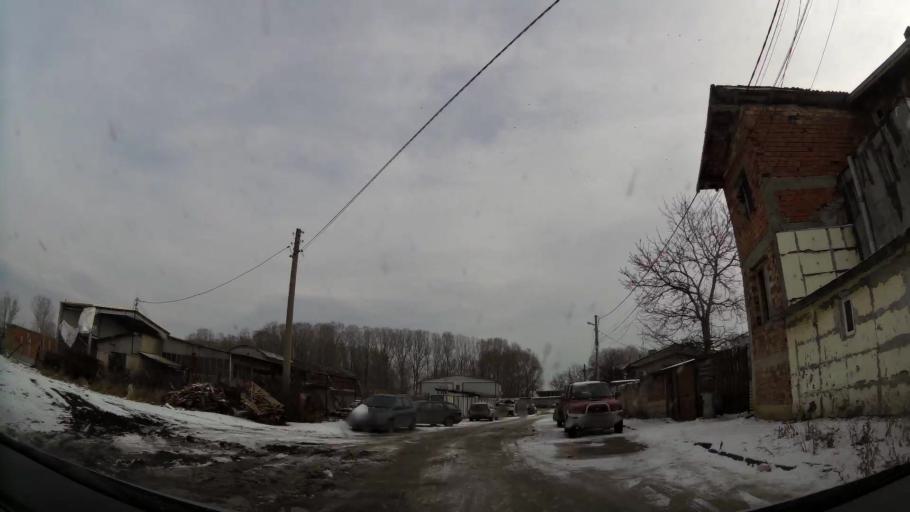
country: BG
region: Sofia-Capital
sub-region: Stolichna Obshtina
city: Sofia
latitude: 42.7153
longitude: 23.4194
